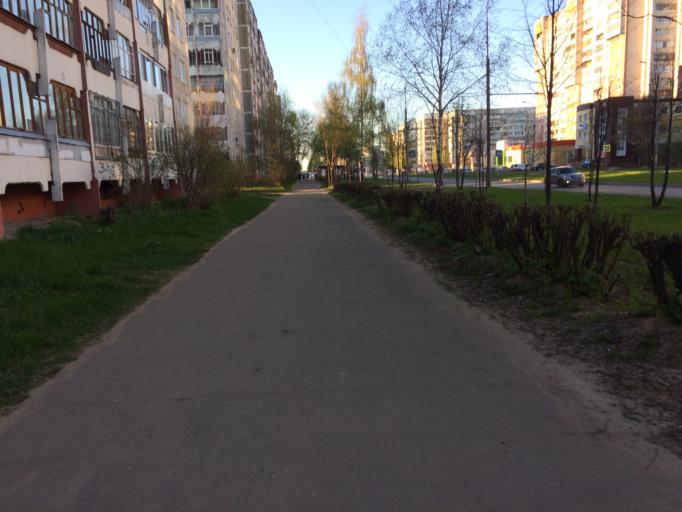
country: RU
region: Mariy-El
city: Yoshkar-Ola
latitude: 56.6286
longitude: 47.9160
